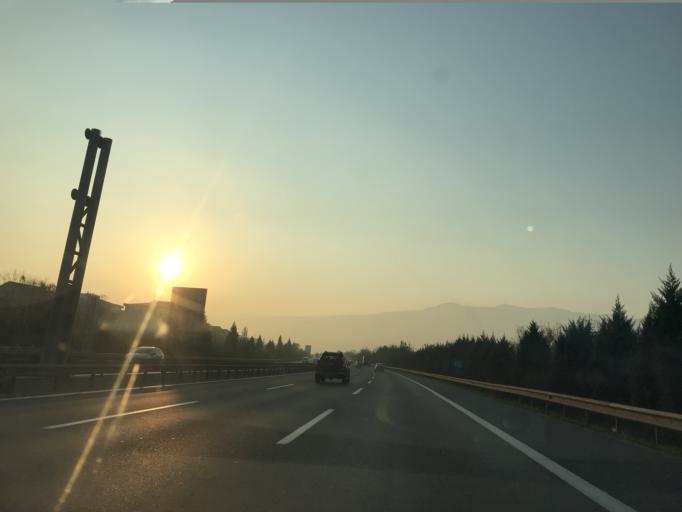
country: TR
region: Kocaeli
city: Kosekoy
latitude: 40.7412
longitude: 30.0446
